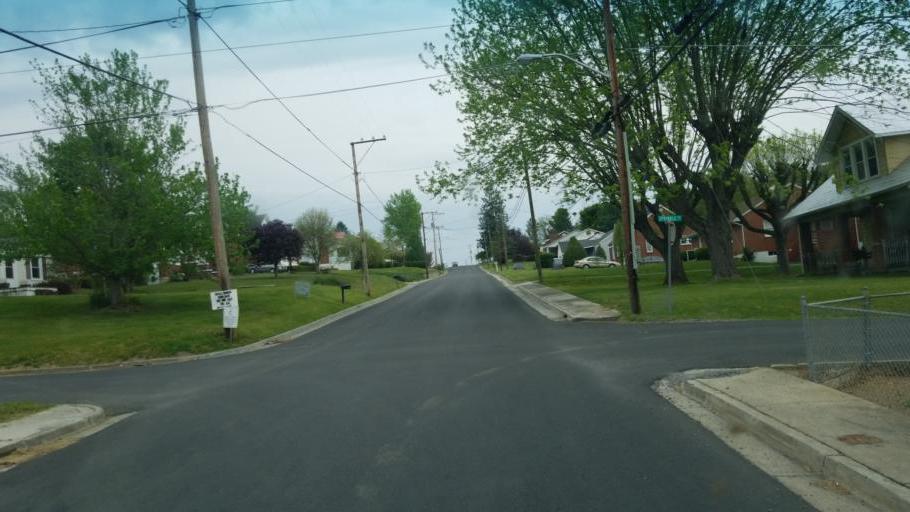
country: US
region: Virginia
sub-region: Smyth County
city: Marion
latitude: 36.8423
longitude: -81.5204
